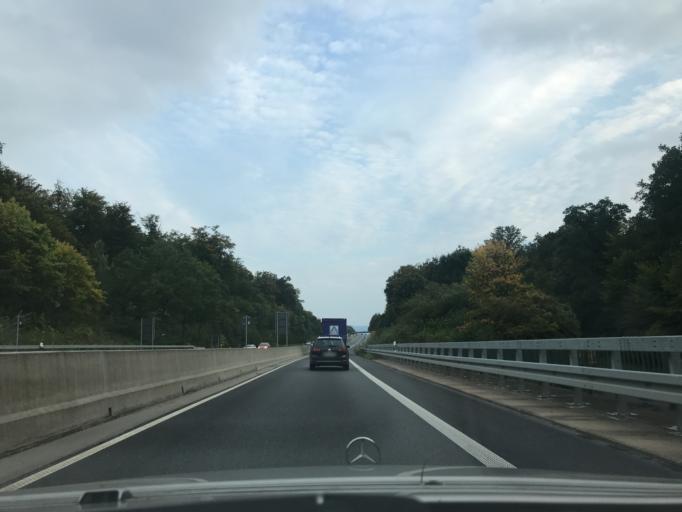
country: DE
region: Hesse
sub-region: Regierungsbezirk Kassel
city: Espenau
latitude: 51.3909
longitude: 9.4338
